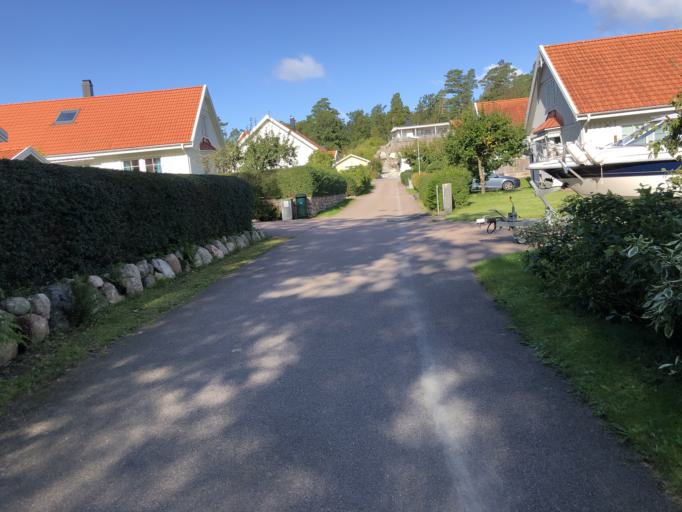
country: SE
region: Vaestra Goetaland
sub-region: Goteborg
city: Torslanda
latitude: 57.7451
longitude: 11.8190
